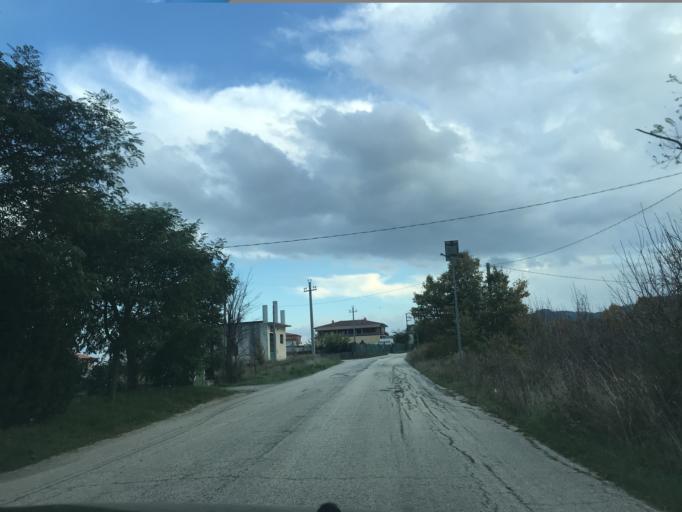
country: IT
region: Molise
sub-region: Provincia di Isernia
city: Bagnoli del Trigno
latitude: 41.6960
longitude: 14.4612
